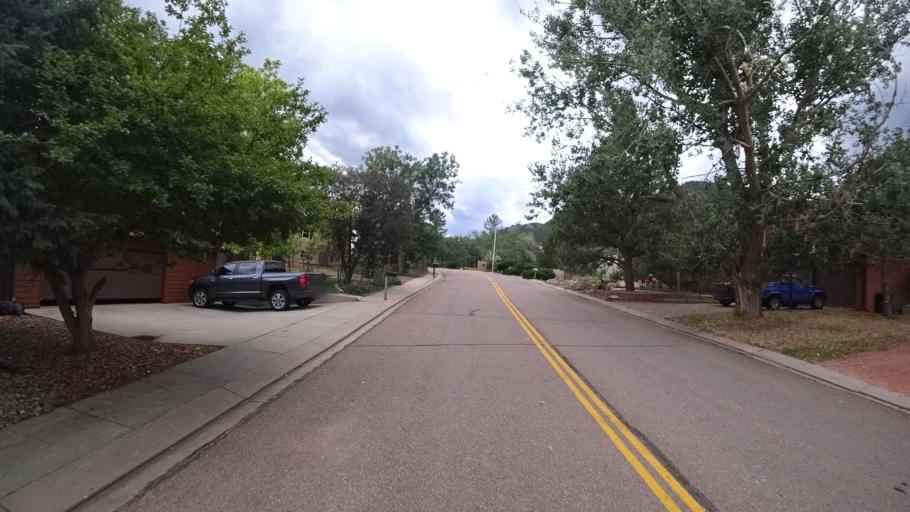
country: US
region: Colorado
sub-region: El Paso County
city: Manitou Springs
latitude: 38.8437
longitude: -104.8977
